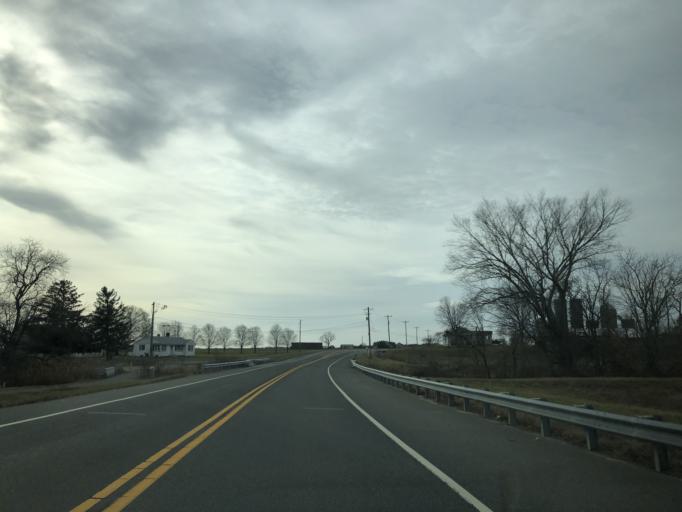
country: US
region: Delaware
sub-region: New Castle County
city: Middletown
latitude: 39.5147
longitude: -75.6786
